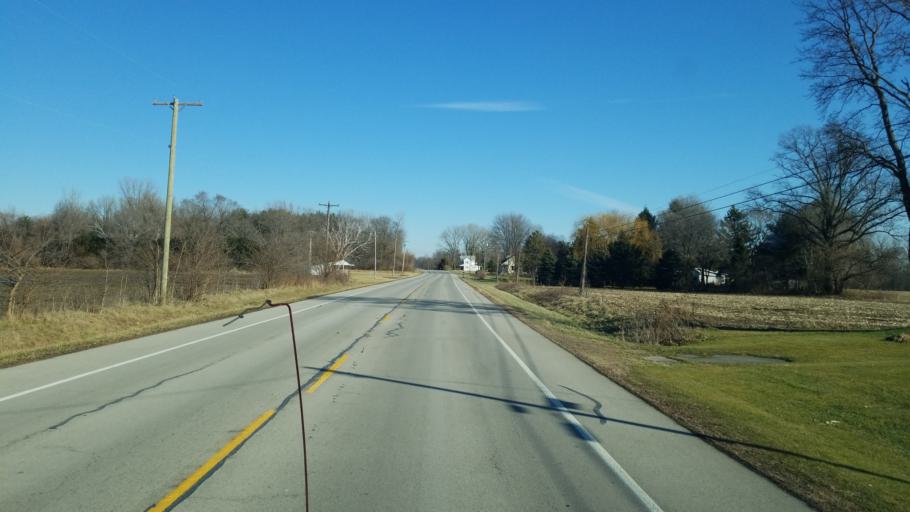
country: US
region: Ohio
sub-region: Lucas County
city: Whitehouse
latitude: 41.4373
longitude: -83.8195
